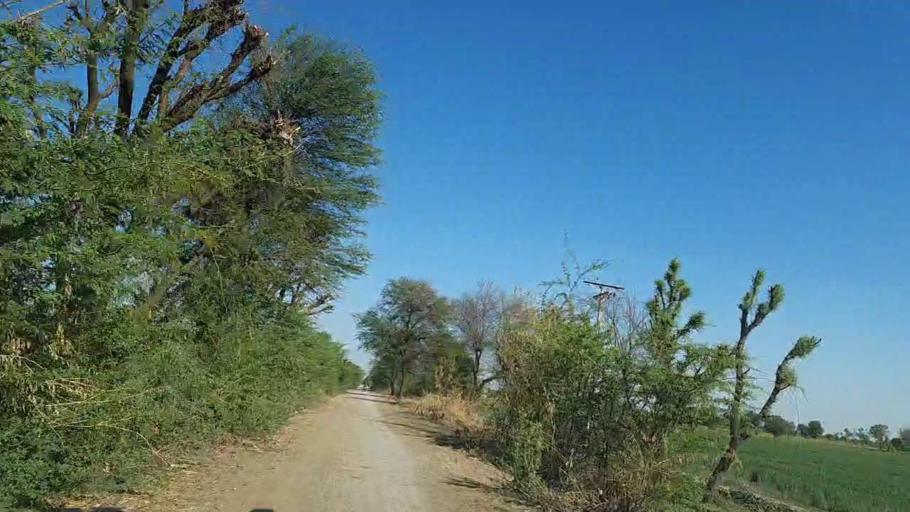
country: PK
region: Sindh
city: Dhoro Naro
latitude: 25.5157
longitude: 69.4807
